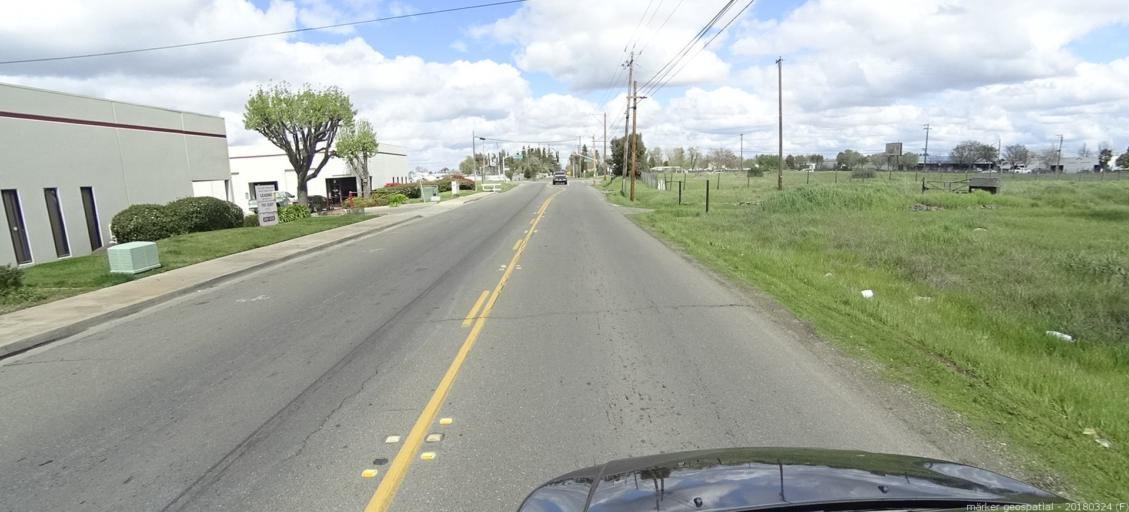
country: US
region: California
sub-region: Sacramento County
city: North Highlands
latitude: 38.6890
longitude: -121.3921
